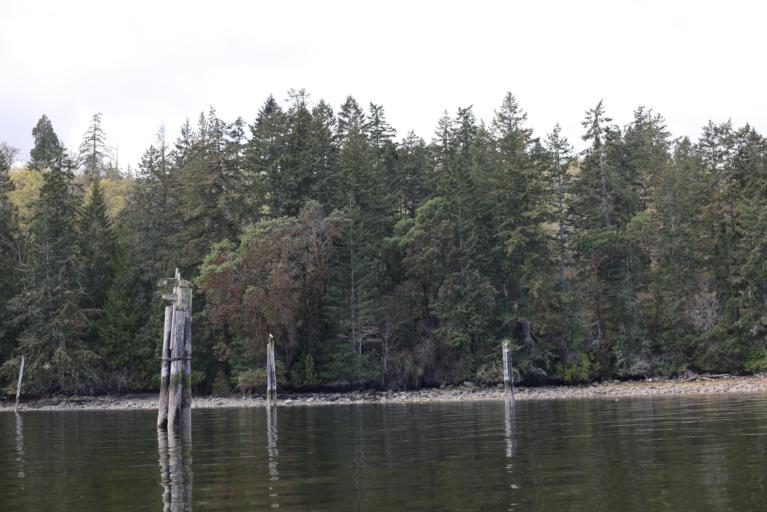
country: CA
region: British Columbia
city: North Saanich
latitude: 48.6274
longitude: -123.5261
